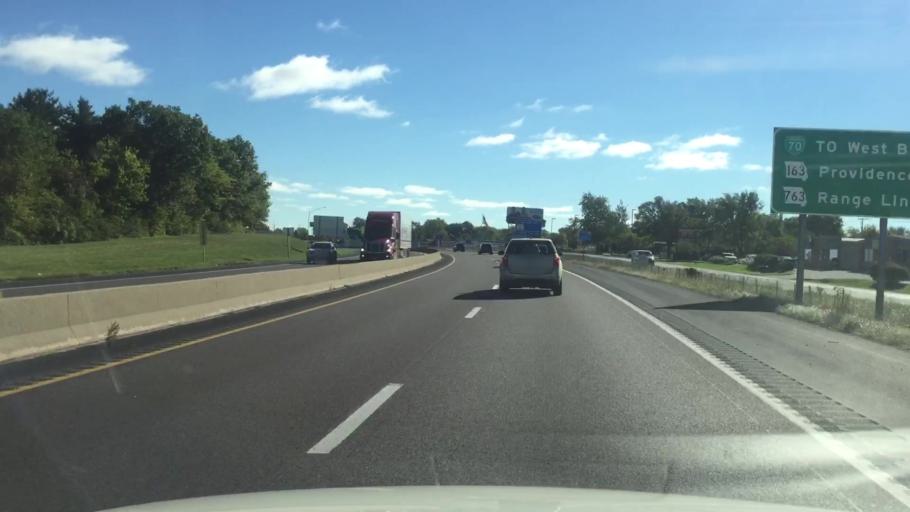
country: US
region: Missouri
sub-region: Boone County
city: Columbia
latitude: 38.9646
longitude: -92.3607
